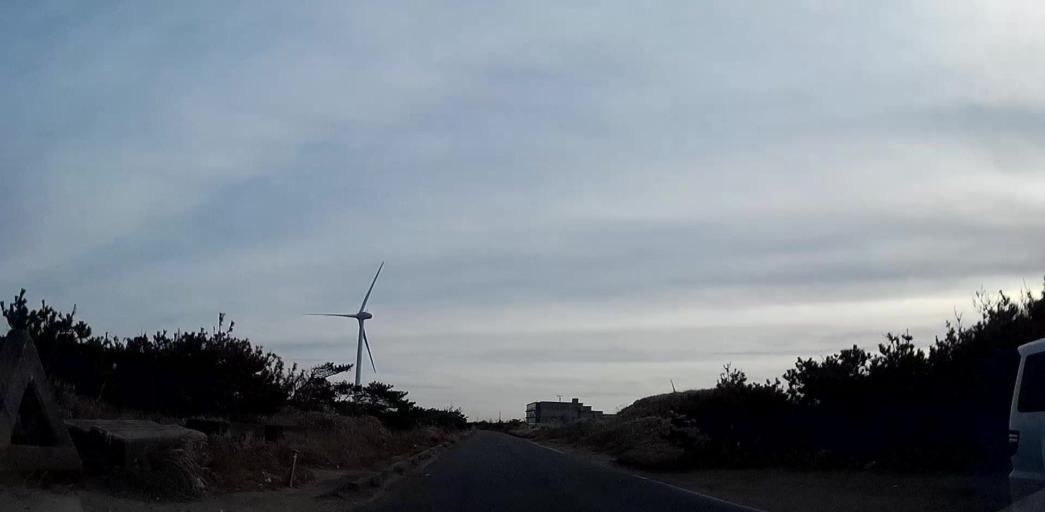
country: JP
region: Chiba
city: Hasaki
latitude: 35.7949
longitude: 140.7945
